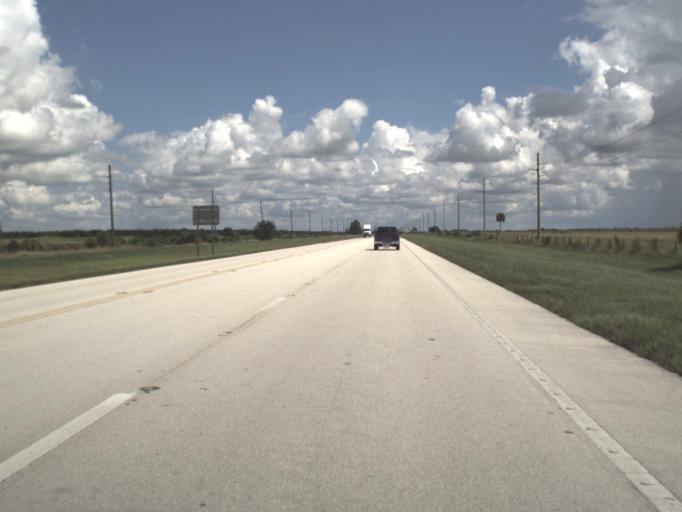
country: US
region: Florida
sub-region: Highlands County
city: Placid Lakes
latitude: 27.2096
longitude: -81.6116
